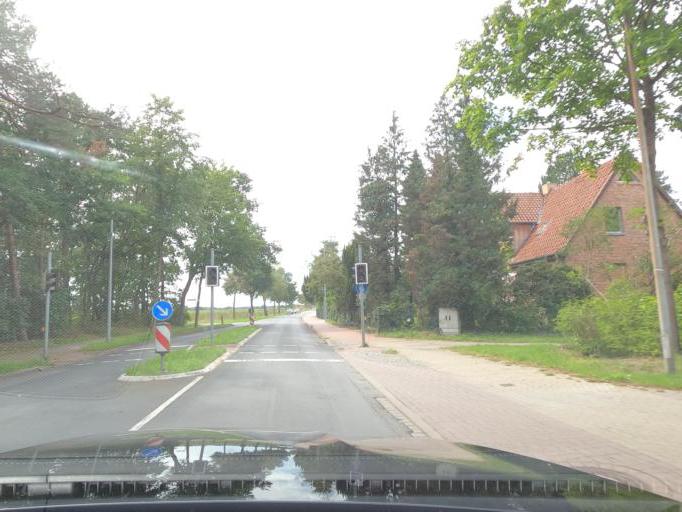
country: DE
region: Lower Saxony
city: Burgdorf
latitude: 52.5148
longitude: 10.0084
